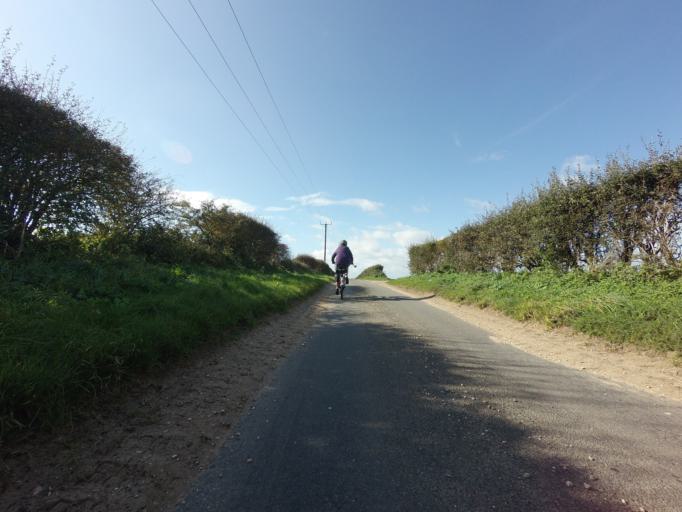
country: GB
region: England
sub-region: Norfolk
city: Hunstanton
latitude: 52.9360
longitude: 0.6025
